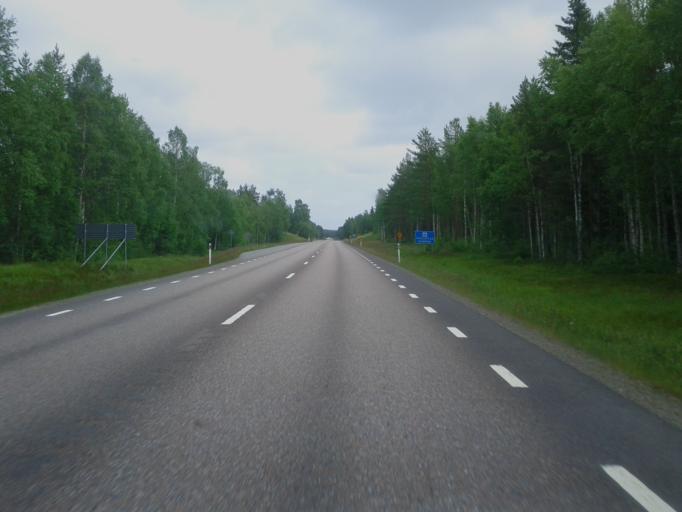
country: SE
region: Vaesterbotten
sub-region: Skelleftea Kommun
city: Burea
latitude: 64.3221
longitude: 21.1835
